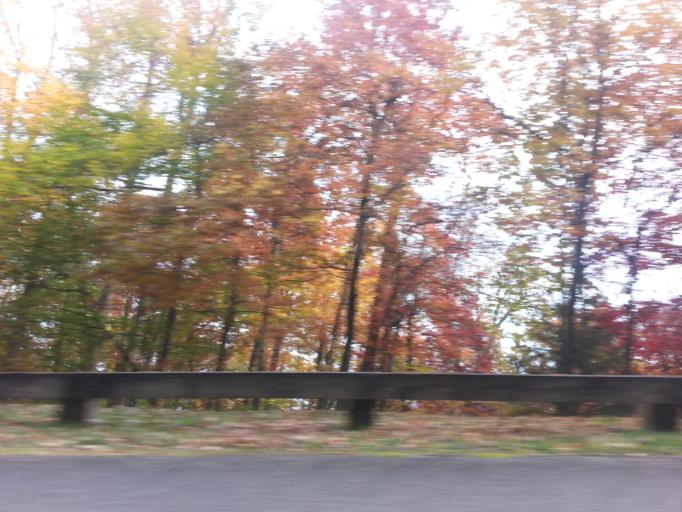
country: US
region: North Carolina
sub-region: Ashe County
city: Jefferson
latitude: 36.2942
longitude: -81.3678
